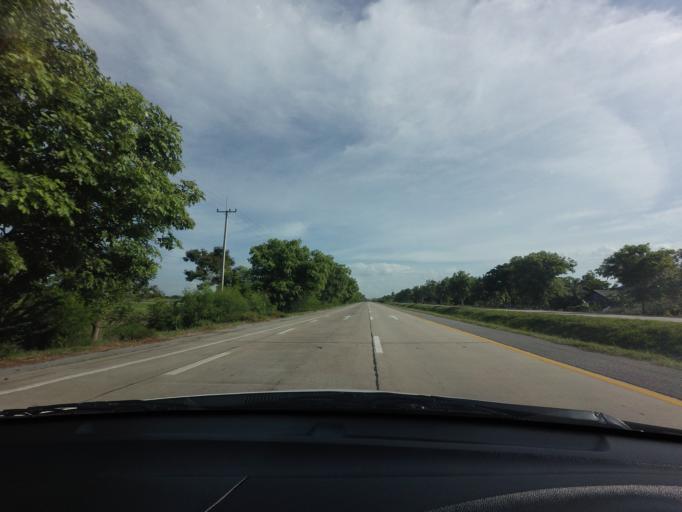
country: TH
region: Suphan Buri
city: Suphan Buri
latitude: 14.4884
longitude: 100.0443
